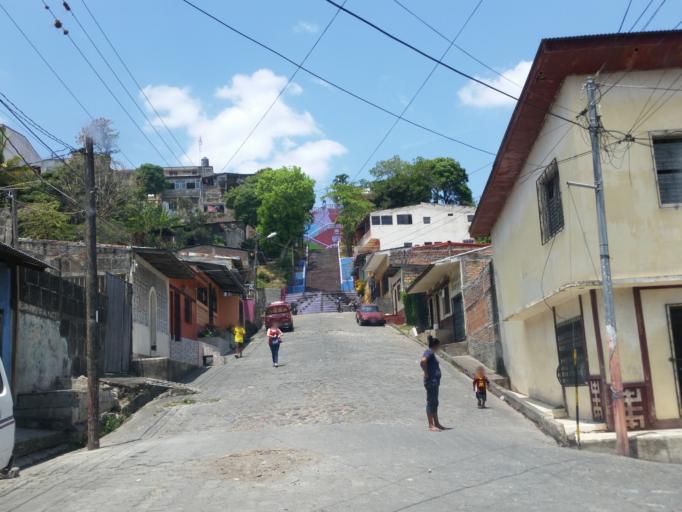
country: NI
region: Boaco
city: Boaco
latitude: 12.4725
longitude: -85.6576
